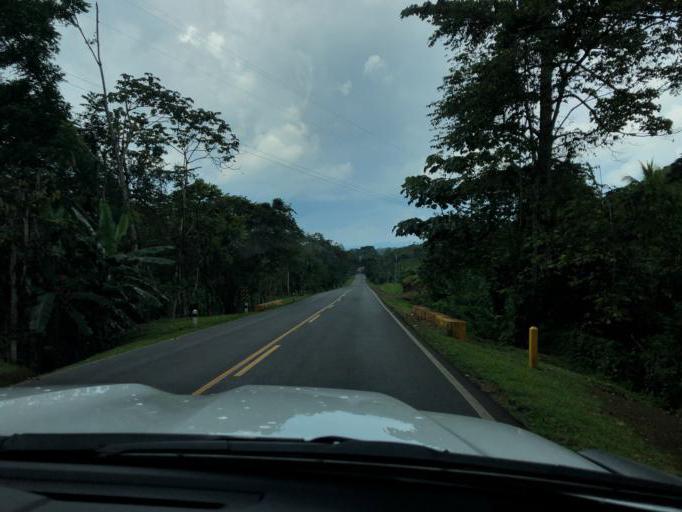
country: NI
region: Chontales
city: Villa Sandino
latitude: 11.9954
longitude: -84.7912
